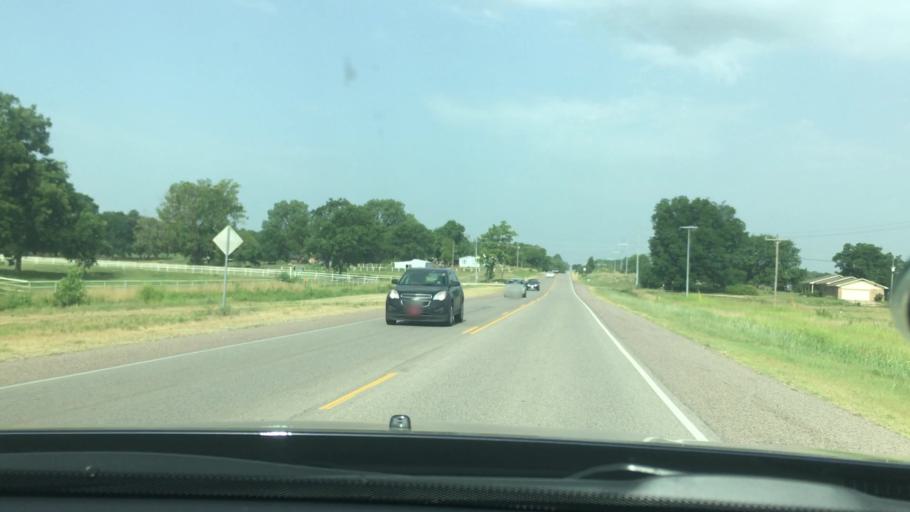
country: US
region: Oklahoma
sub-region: Pontotoc County
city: Ada
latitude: 34.7821
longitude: -96.7586
